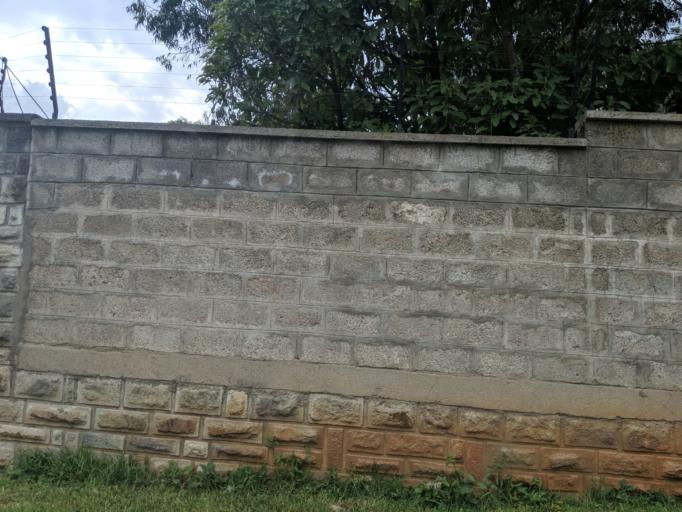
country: ET
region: Adis Abeba
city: Addis Ababa
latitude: 8.9947
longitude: 38.7812
